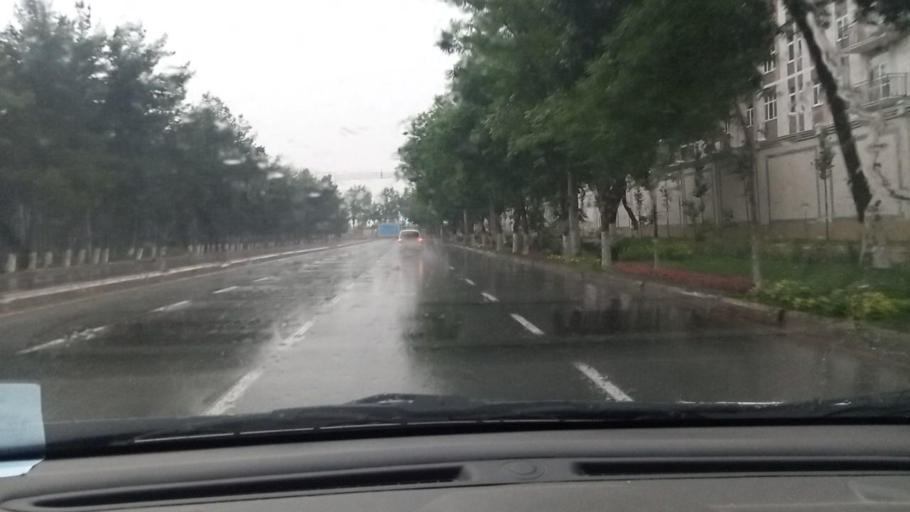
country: UZ
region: Toshkent
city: Salor
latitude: 41.3246
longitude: 69.3620
